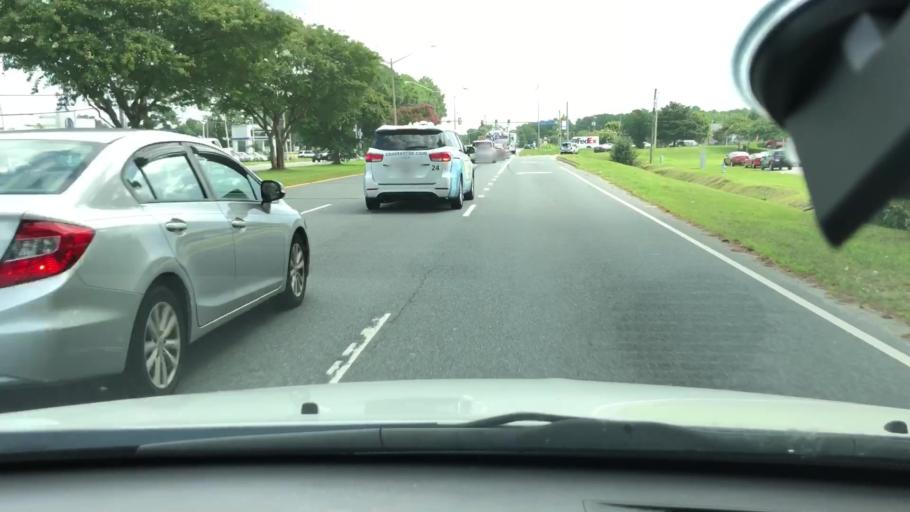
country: US
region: Virginia
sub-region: City of Chesapeake
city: Chesapeake
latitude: 36.7922
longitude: -76.2407
